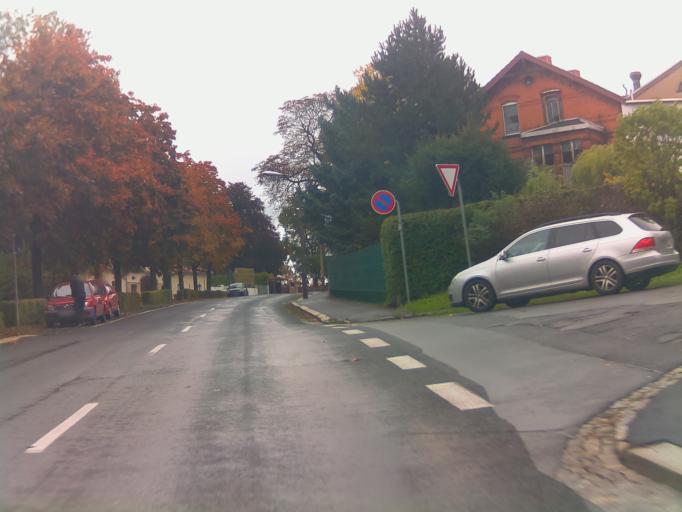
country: DE
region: Thuringia
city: Possneck
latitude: 50.6905
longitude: 11.5967
